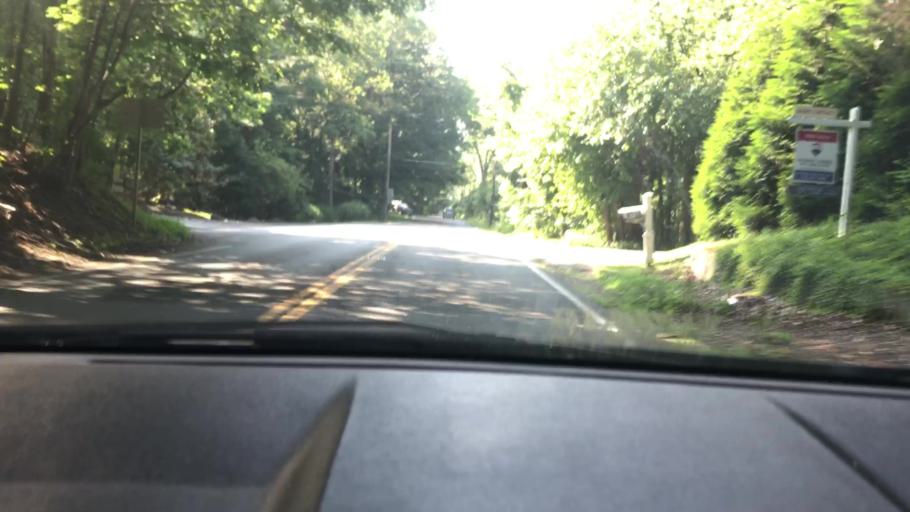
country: US
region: Virginia
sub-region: Fairfax County
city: Wolf Trap
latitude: 38.9691
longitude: -77.2486
